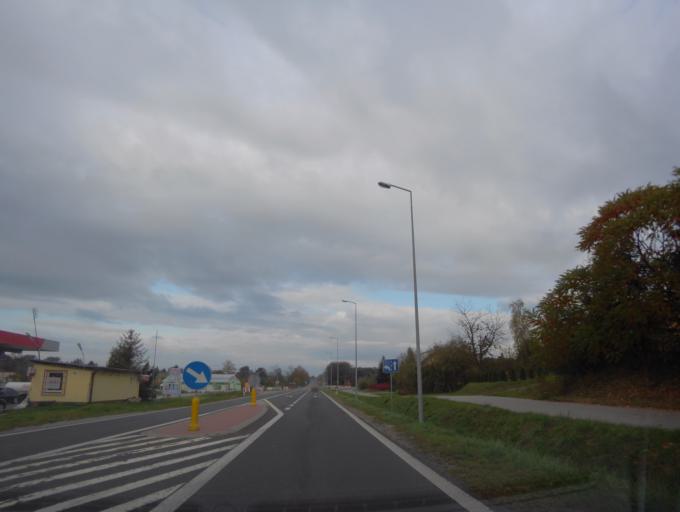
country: PL
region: Lublin Voivodeship
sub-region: Powiat bilgorajski
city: Goraj
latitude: 50.7180
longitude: 22.6747
